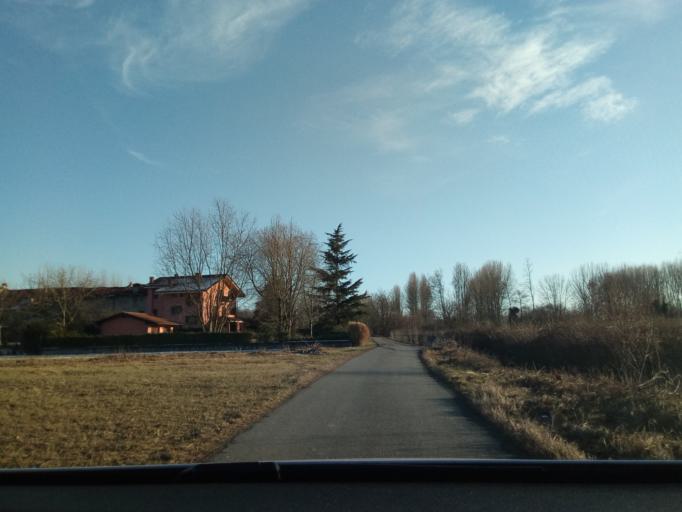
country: IT
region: Piedmont
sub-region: Provincia di Torino
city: Bollengo
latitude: 45.4626
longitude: 7.9317
